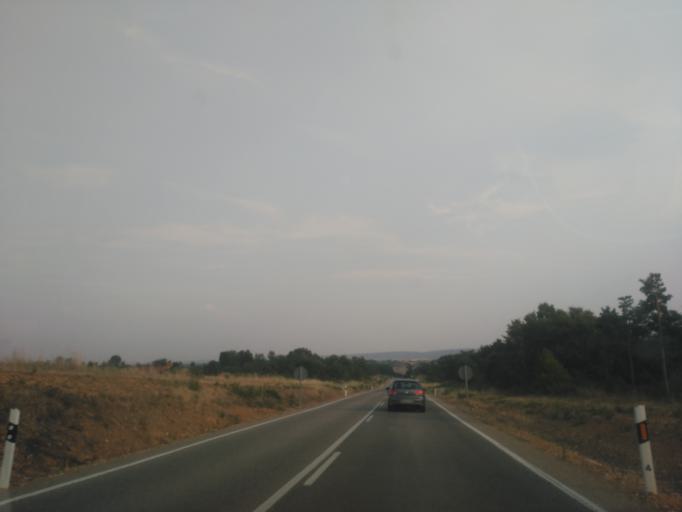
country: ES
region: Castille and Leon
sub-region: Provincia de Zamora
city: Tabara
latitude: 41.8418
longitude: -5.9765
